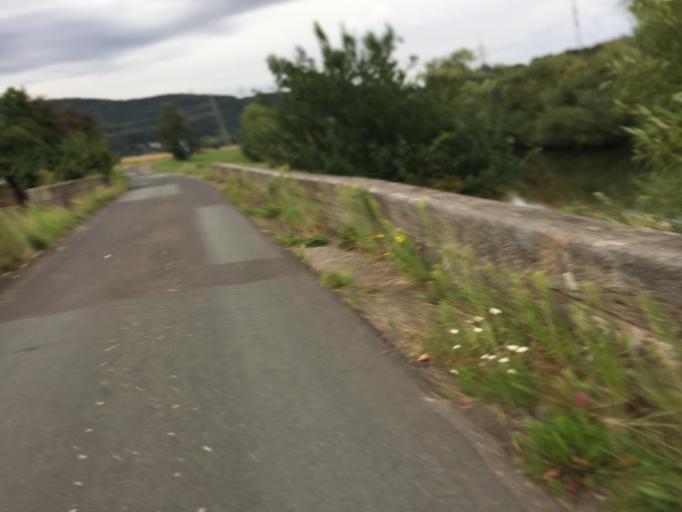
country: DE
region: Hesse
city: Breitenbach
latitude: 50.9086
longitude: 9.7524
